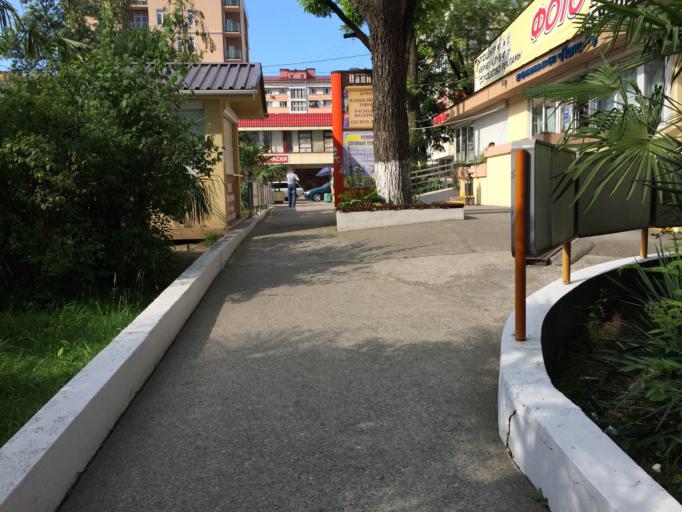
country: RU
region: Krasnodarskiy
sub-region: Sochi City
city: Sochi
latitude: 43.5946
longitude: 39.7268
